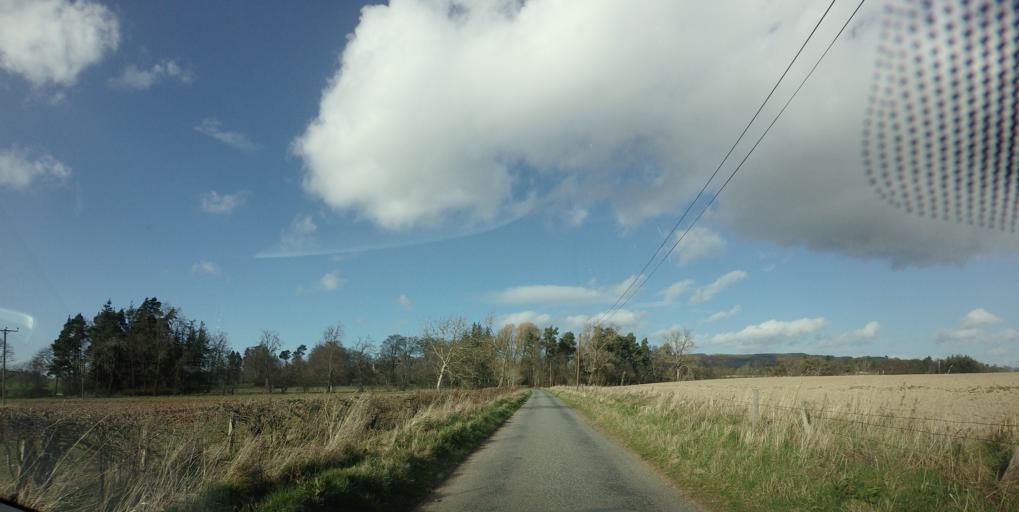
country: GB
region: Scotland
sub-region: Perth and Kinross
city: Bridge of Earn
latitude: 56.3355
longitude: -3.4290
